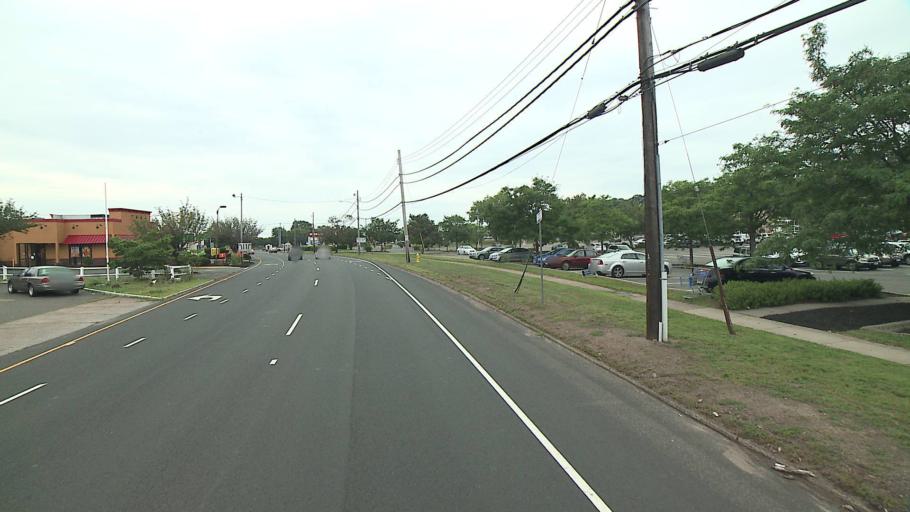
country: US
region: Connecticut
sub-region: New Haven County
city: Hamden
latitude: 41.3763
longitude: -72.9157
